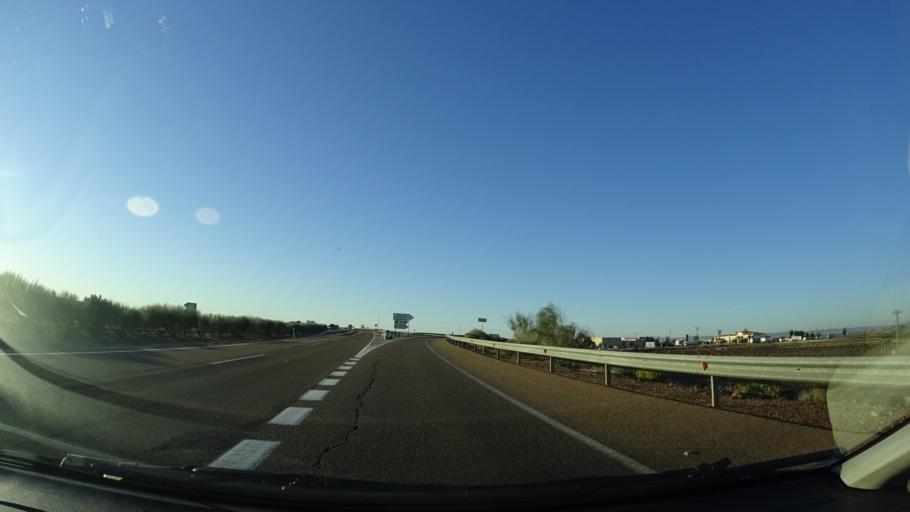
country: ES
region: Extremadura
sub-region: Provincia de Badajoz
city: Almendralejo
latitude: 38.7131
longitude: -6.3962
